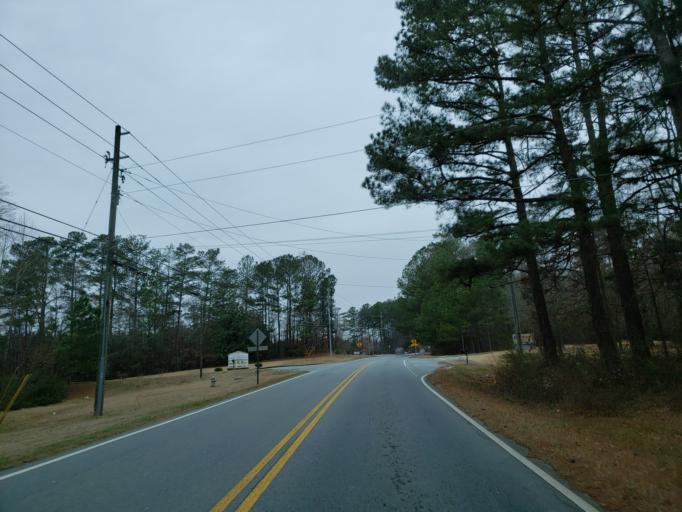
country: US
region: Georgia
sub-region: Cobb County
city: Powder Springs
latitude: 33.9233
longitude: -84.6509
